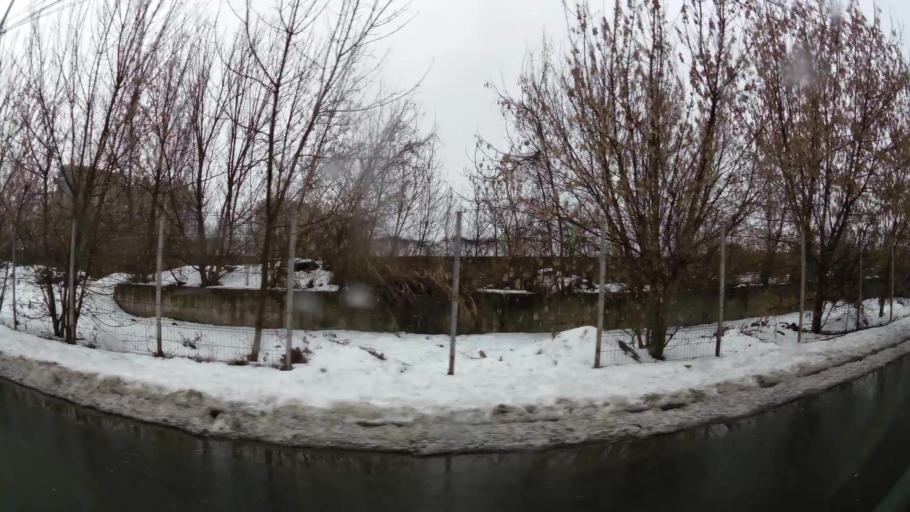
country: RO
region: Ilfov
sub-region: Comuna Mogosoaia
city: Mogosoaia
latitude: 44.4987
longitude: 26.0334
